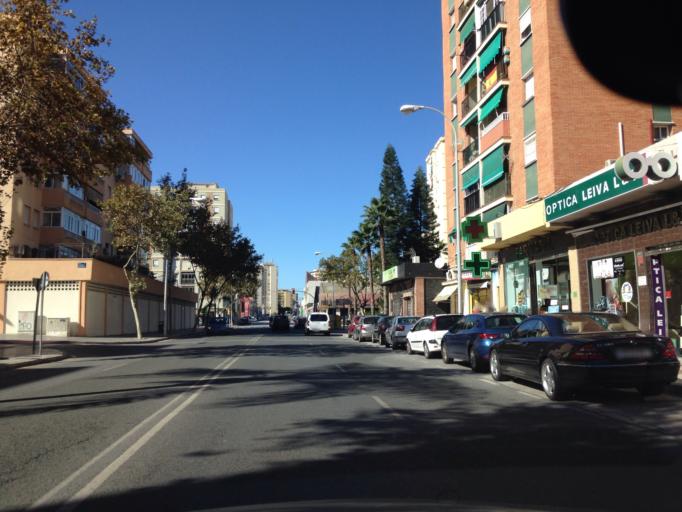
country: ES
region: Andalusia
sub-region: Provincia de Malaga
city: Malaga
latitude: 36.6915
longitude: -4.4488
